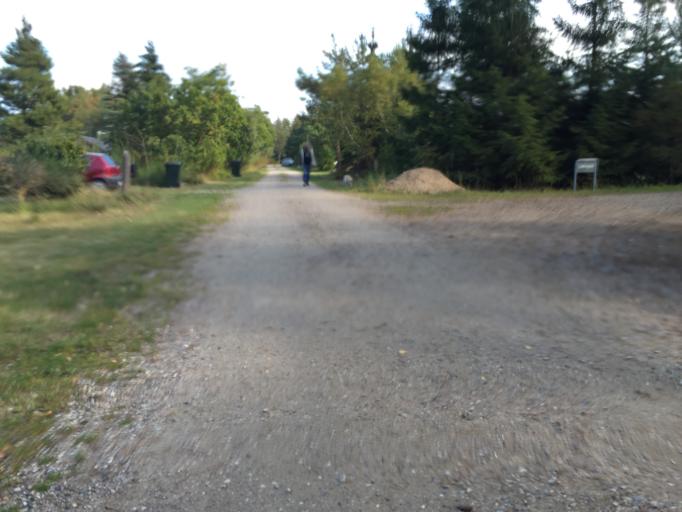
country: DK
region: Zealand
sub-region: Odsherred Kommune
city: Hojby
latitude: 55.9011
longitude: 11.5553
